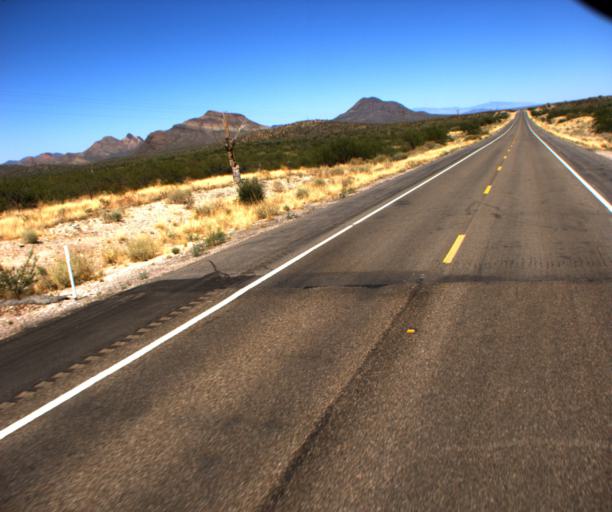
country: US
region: Arizona
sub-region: Pima County
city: Three Points
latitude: 32.0366
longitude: -111.5325
